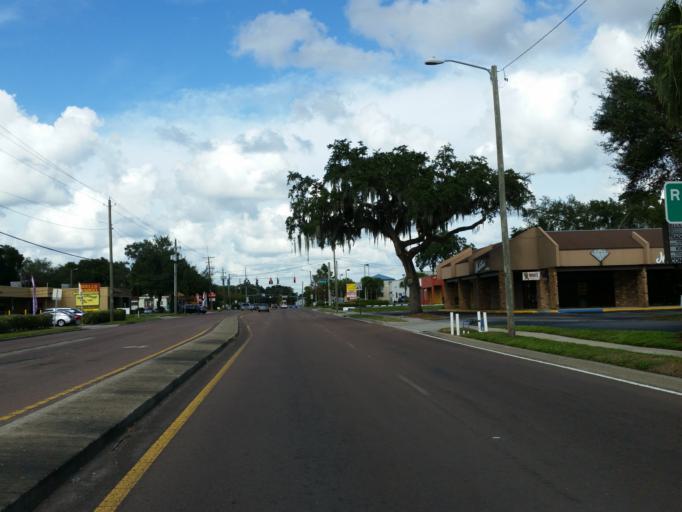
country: US
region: Florida
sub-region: Hillsborough County
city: Brandon
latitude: 27.9346
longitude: -82.2938
